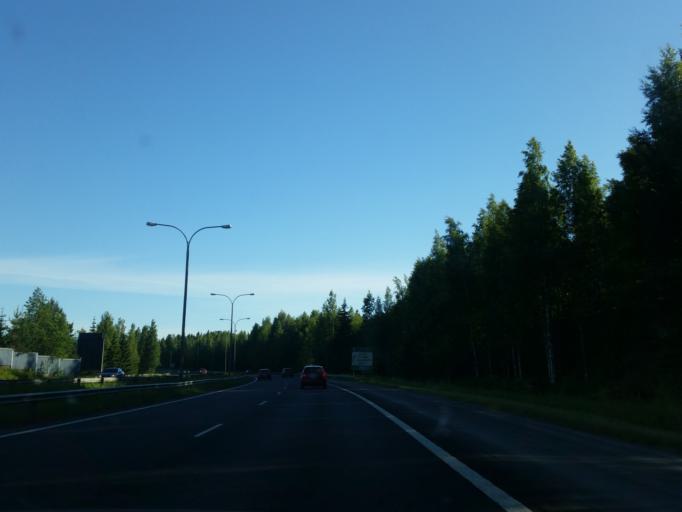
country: FI
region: Northern Savo
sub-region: Kuopio
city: Kuopio
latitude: 62.8764
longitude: 27.6236
